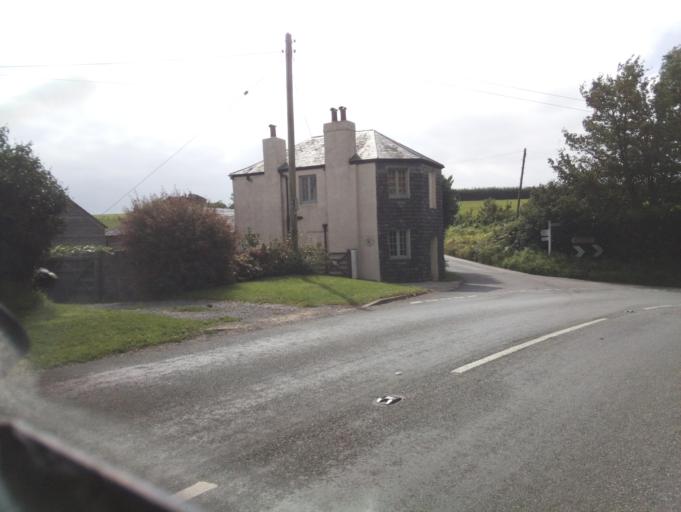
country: GB
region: England
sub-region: Devon
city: Dartmouth
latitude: 50.3649
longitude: -3.5516
